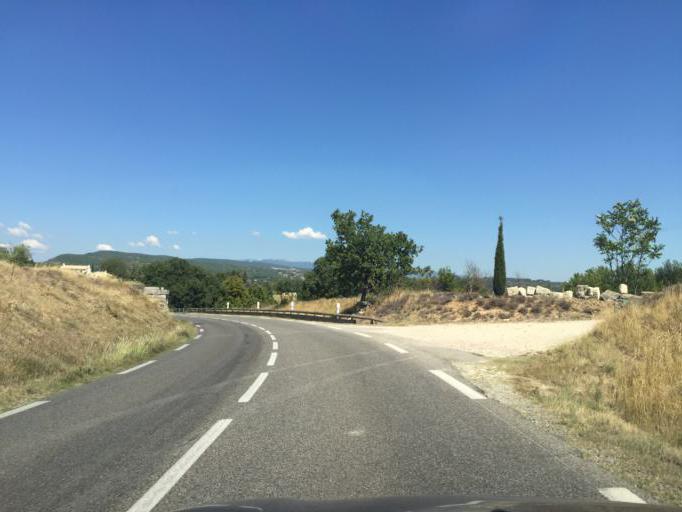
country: FR
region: Provence-Alpes-Cote d'Azur
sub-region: Departement des Alpes-de-Haute-Provence
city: Mane
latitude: 43.9198
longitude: 5.7569
